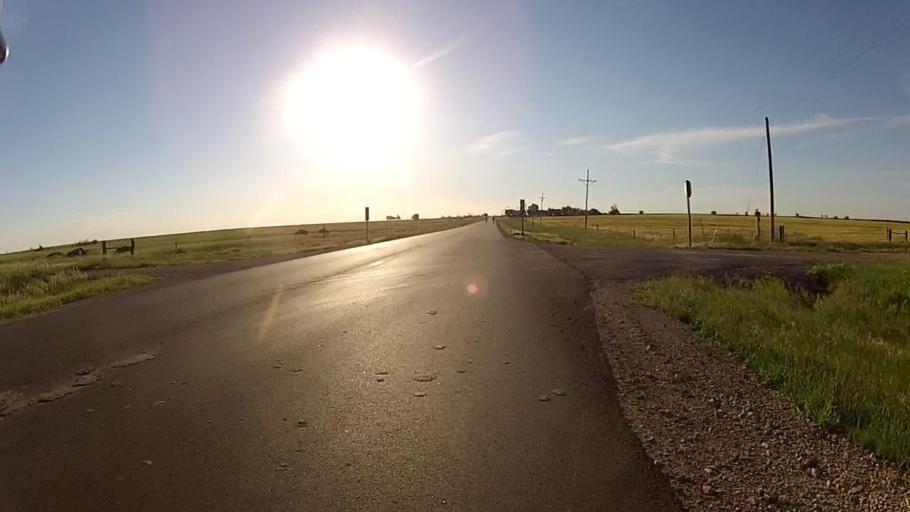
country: US
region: Kansas
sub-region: Comanche County
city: Coldwater
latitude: 37.2819
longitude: -99.1472
